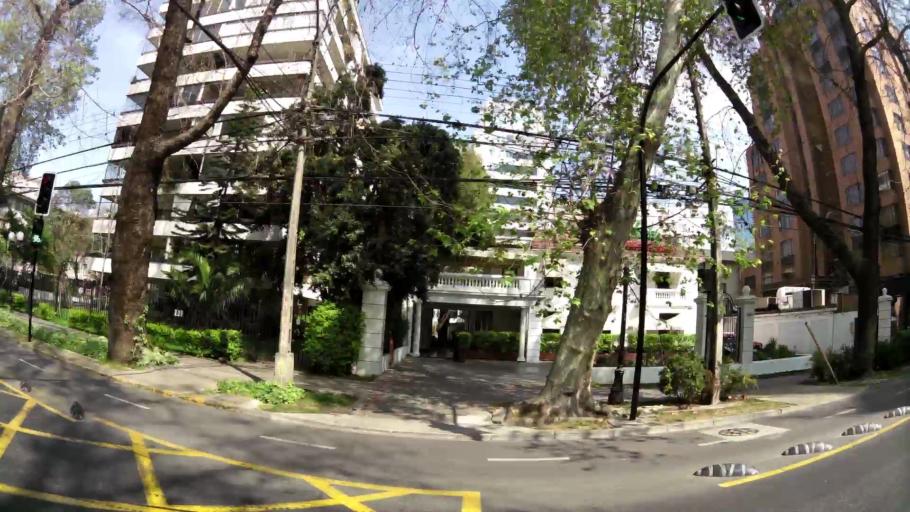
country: CL
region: Santiago Metropolitan
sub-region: Provincia de Santiago
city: Villa Presidente Frei, Nunoa, Santiago, Chile
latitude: -33.4240
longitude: -70.6091
